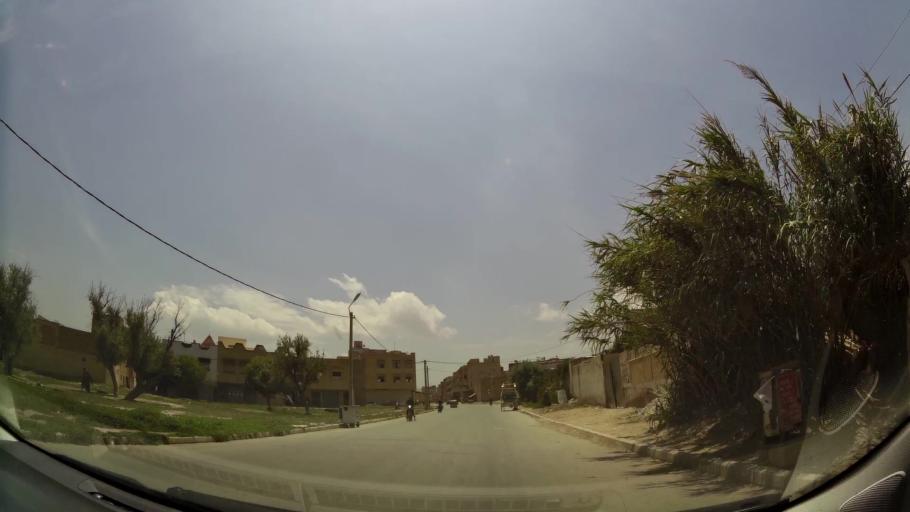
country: MA
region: Oriental
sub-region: Oujda-Angad
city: Oujda
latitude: 34.6833
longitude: -1.8933
